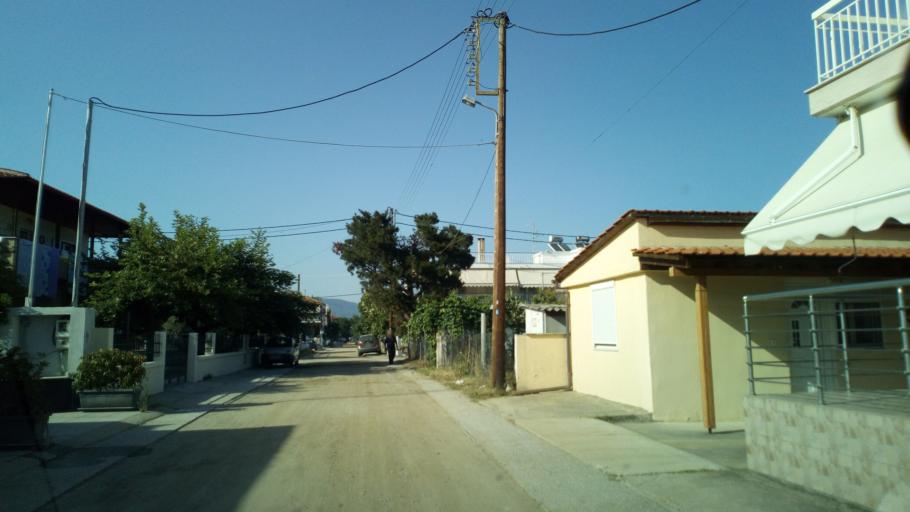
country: GR
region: Central Macedonia
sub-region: Nomos Thessalonikis
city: Nea Vrasna
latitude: 40.7047
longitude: 23.6994
